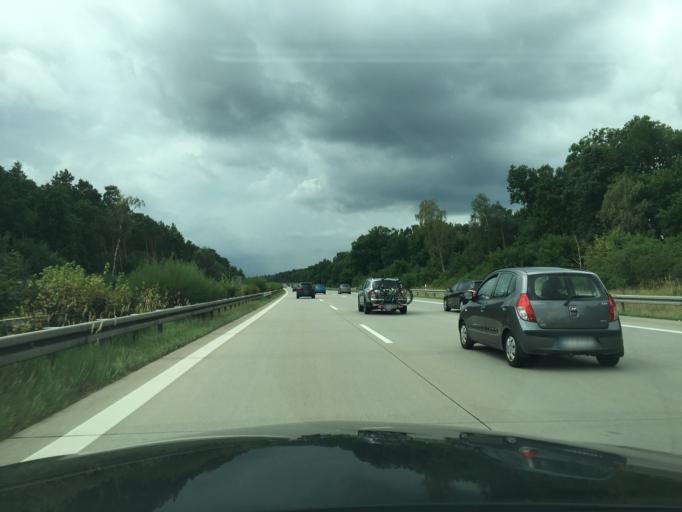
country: DE
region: Brandenburg
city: Niemegk
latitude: 52.0801
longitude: 12.6675
